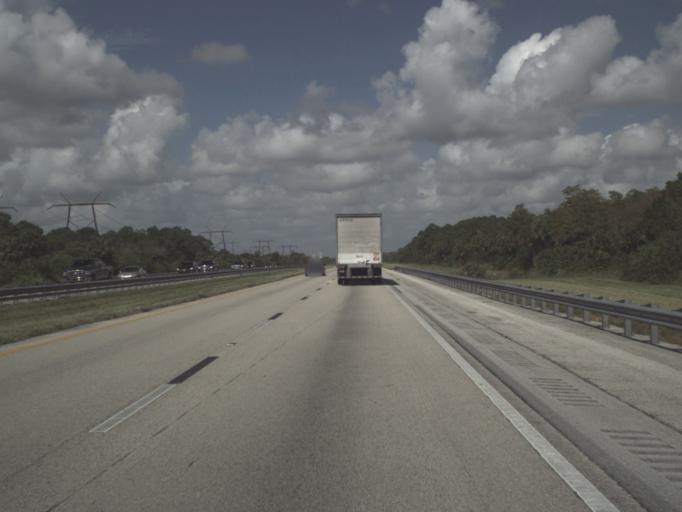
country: US
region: Florida
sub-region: Indian River County
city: West Vero Corridor
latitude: 27.5472
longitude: -80.6287
